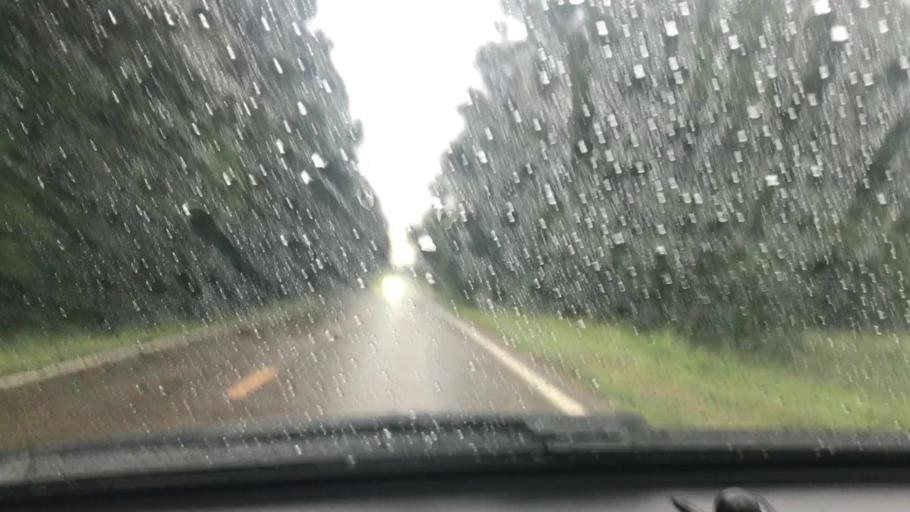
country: US
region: Mississippi
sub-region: Pike County
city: Summit
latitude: 31.3218
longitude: -90.5405
